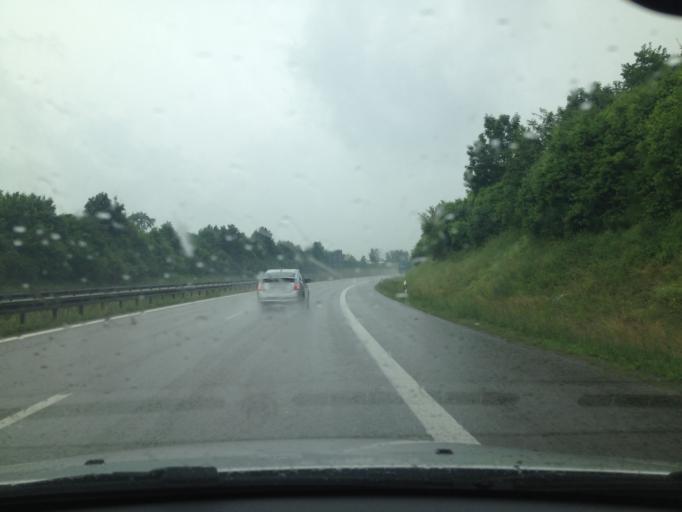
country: DE
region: Bavaria
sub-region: Swabia
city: Klosterlechfeld
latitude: 48.1628
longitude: 10.8366
